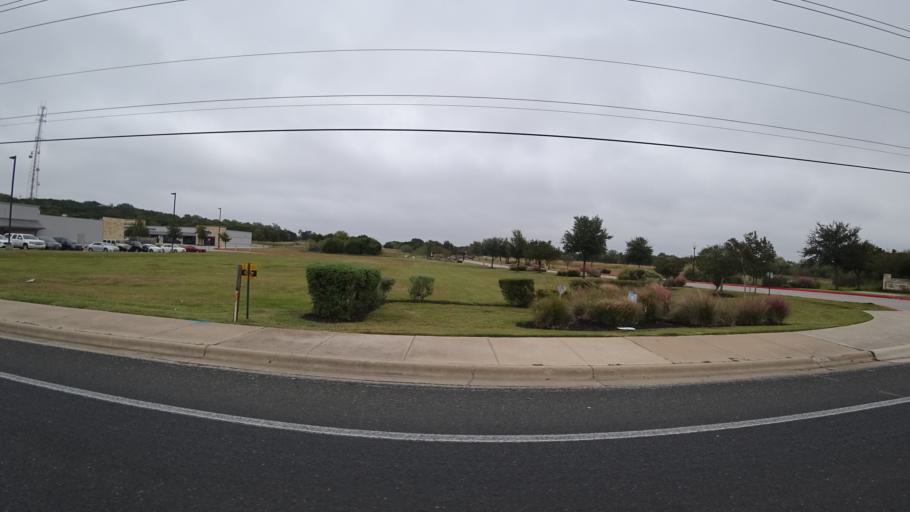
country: US
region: Texas
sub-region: Travis County
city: Shady Hollow
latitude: 30.1930
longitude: -97.8437
